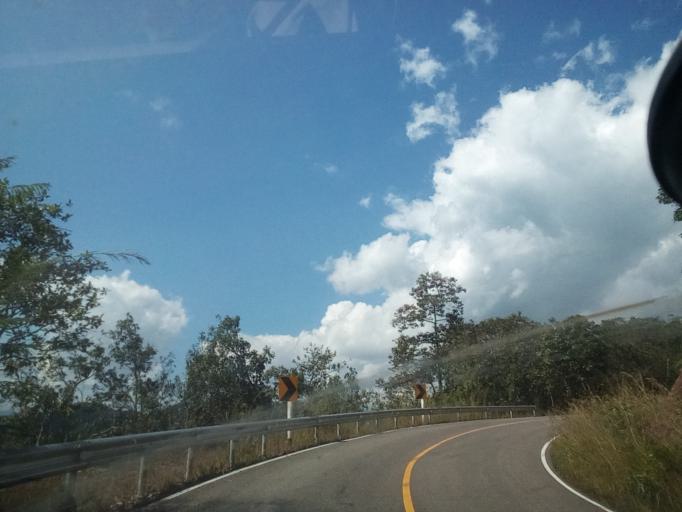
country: TH
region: Chiang Mai
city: Samoeng
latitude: 18.8704
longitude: 98.6911
